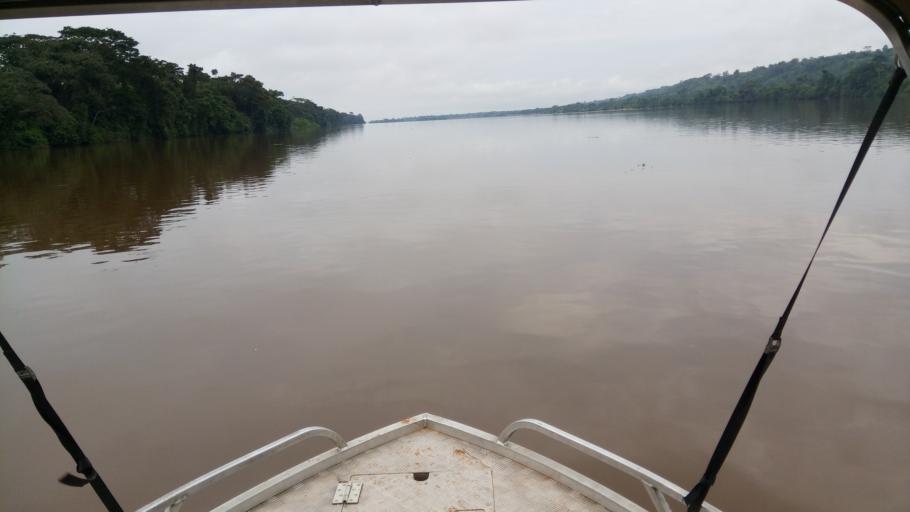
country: CD
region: Eastern Province
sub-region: Sous-Region de la Tshopo
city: Yangambi
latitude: 0.7573
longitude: 24.4646
